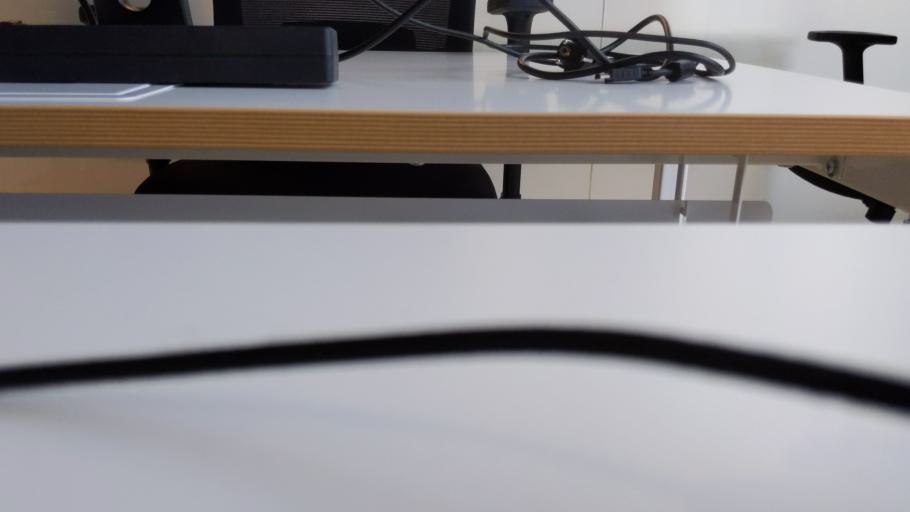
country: RU
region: Moskovskaya
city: Shevlyakovo
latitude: 56.4045
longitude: 36.8988
